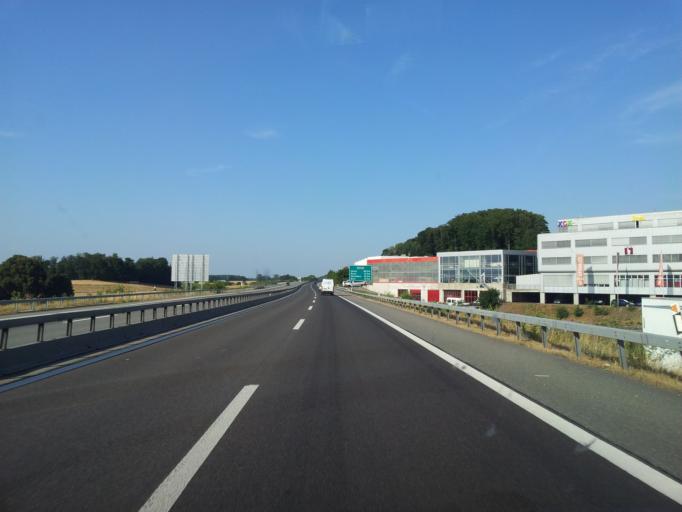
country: CH
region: Fribourg
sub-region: Sense District
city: Dudingen
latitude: 46.8592
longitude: 7.1994
